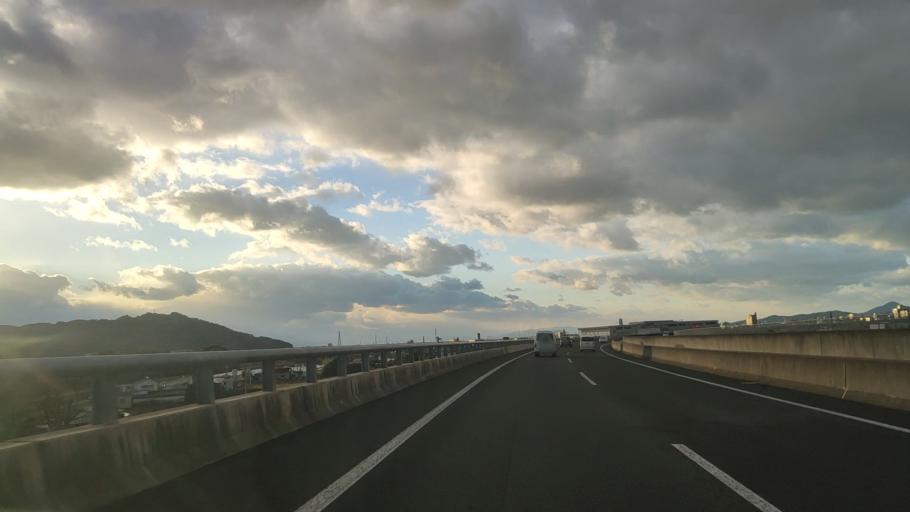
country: JP
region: Ehime
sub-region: Shikoku-chuo Shi
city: Matsuyama
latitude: 33.7881
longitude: 132.8092
